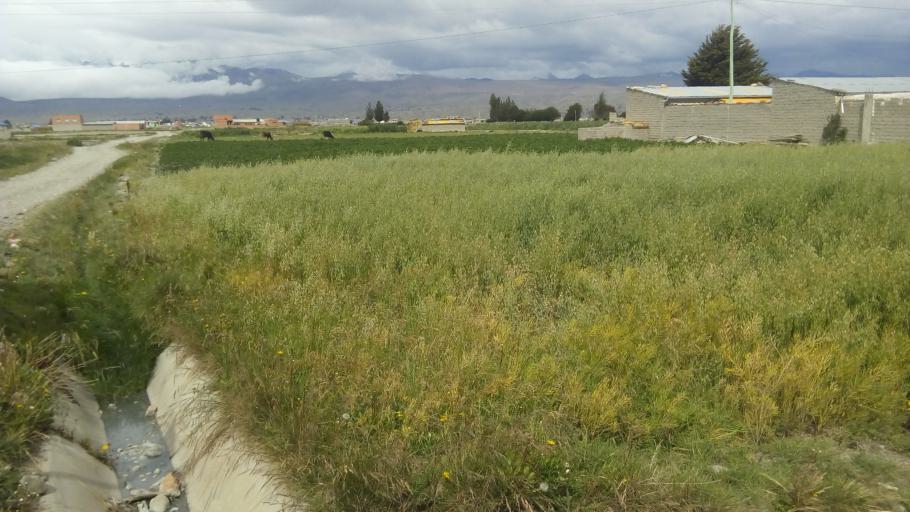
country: BO
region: La Paz
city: Achacachi
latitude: -16.0347
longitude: -68.6806
